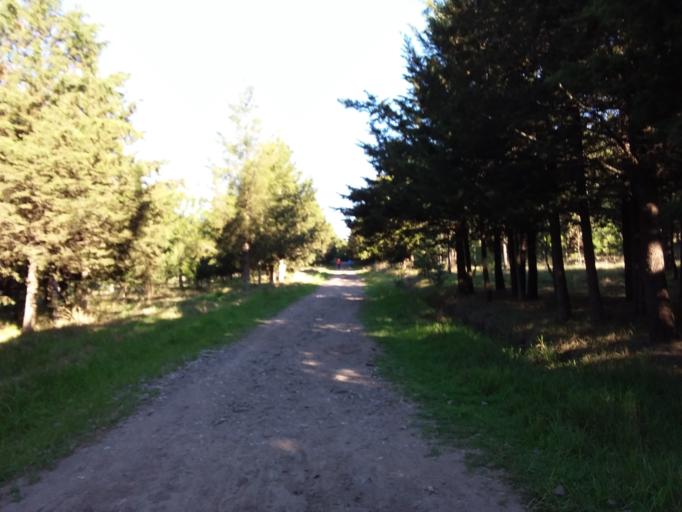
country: MX
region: Mexico
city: San Marcos Yachihuacaltepec
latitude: 19.3113
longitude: -99.6907
